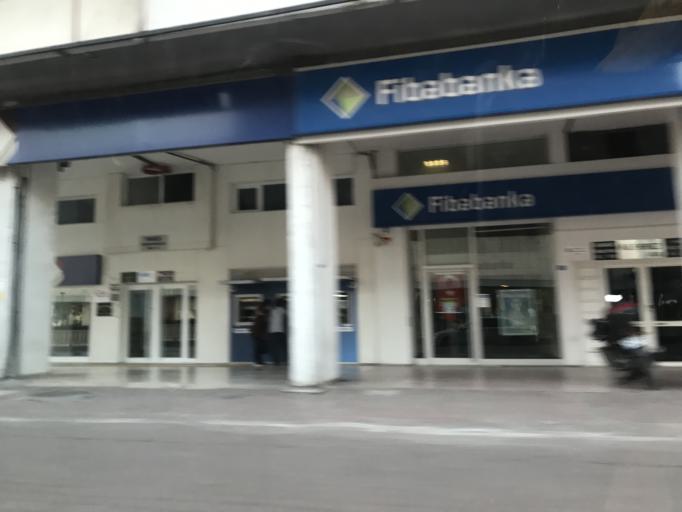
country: TR
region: Antalya
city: Antalya
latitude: 36.8936
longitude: 30.7036
